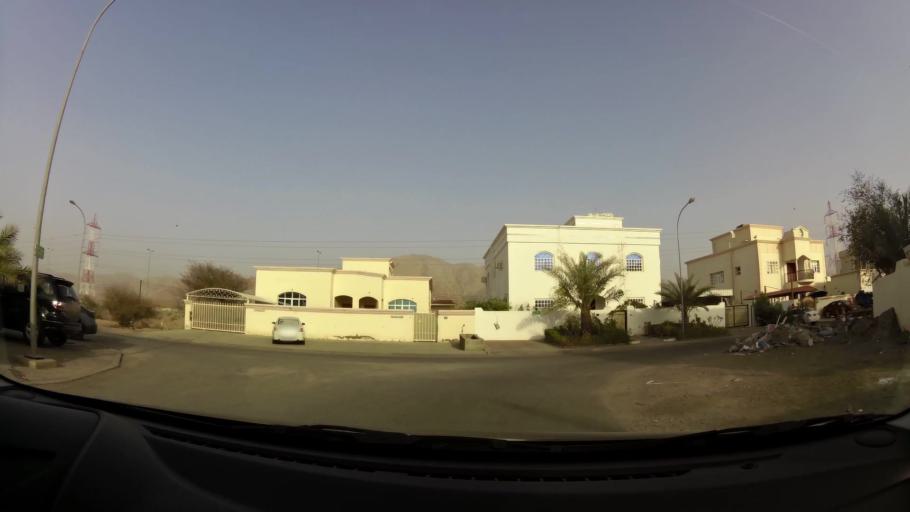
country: OM
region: Muhafazat Masqat
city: Bawshar
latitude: 23.5283
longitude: 58.3500
